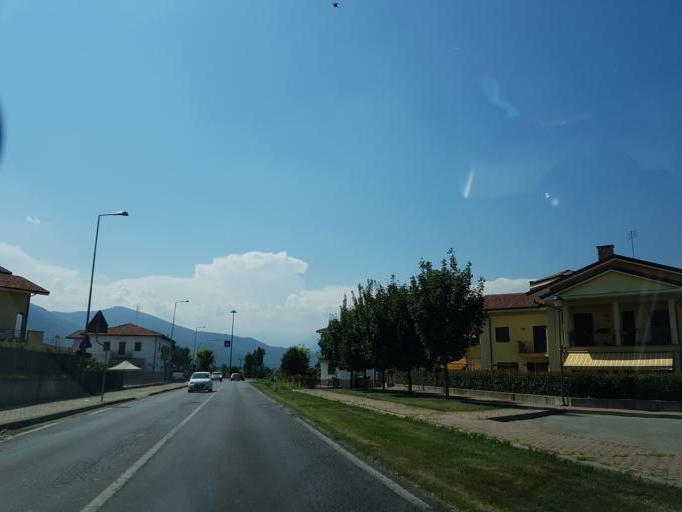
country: IT
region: Piedmont
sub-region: Provincia di Cuneo
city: San Rocco
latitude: 44.3980
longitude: 7.4740
